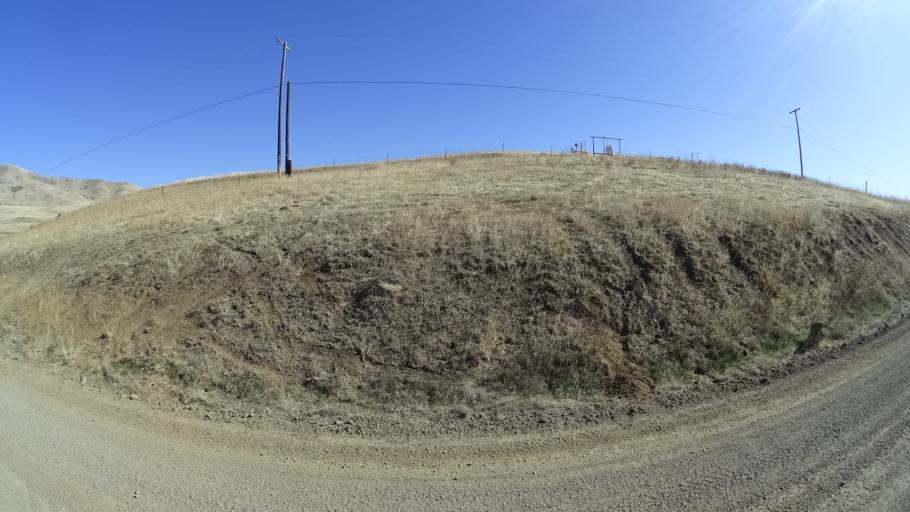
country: US
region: California
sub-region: Siskiyou County
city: Montague
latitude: 41.8310
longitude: -122.4210
